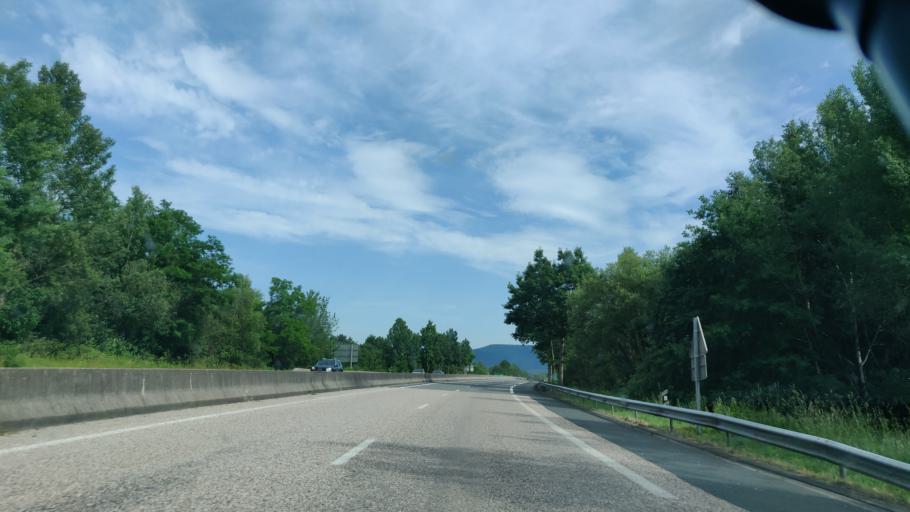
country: FR
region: Lorraine
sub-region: Departement de Meurthe-et-Moselle
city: Baccarat
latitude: 48.4350
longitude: 6.7807
